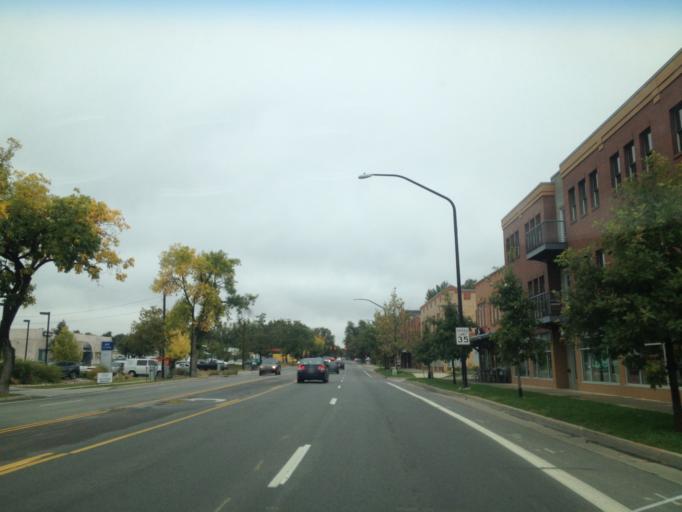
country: US
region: Colorado
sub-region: Boulder County
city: Boulder
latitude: 40.0262
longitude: -105.2536
